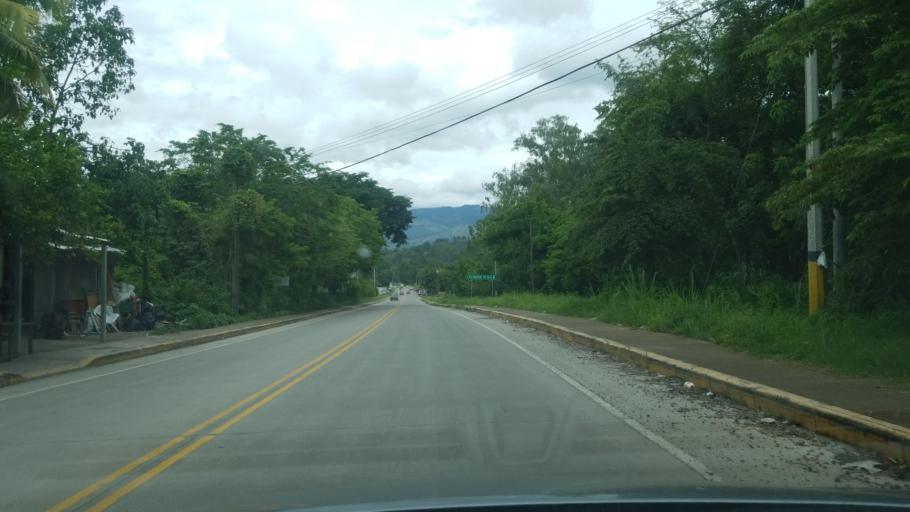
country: HN
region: Copan
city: La Entrada
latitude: 15.0667
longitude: -88.7599
